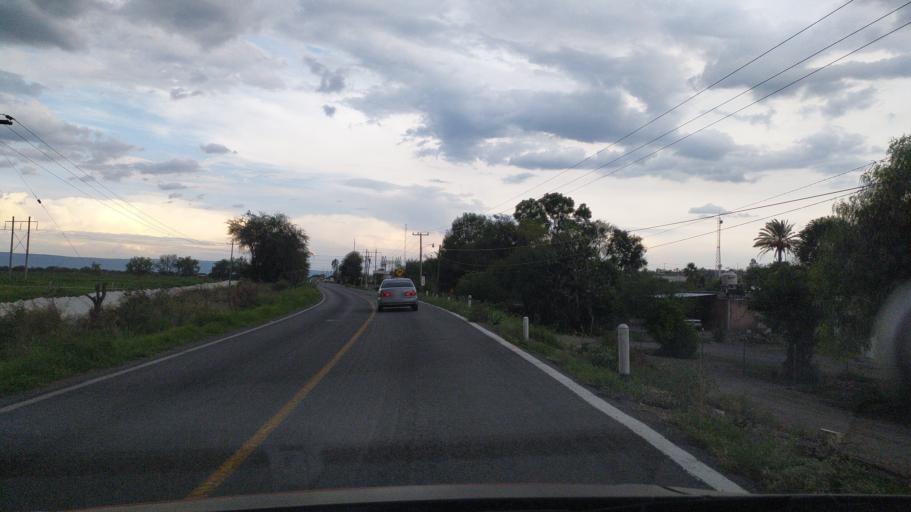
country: MX
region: Guanajuato
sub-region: San Francisco del Rincon
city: San Ignacio de Hidalgo
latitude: 20.8295
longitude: -101.9035
